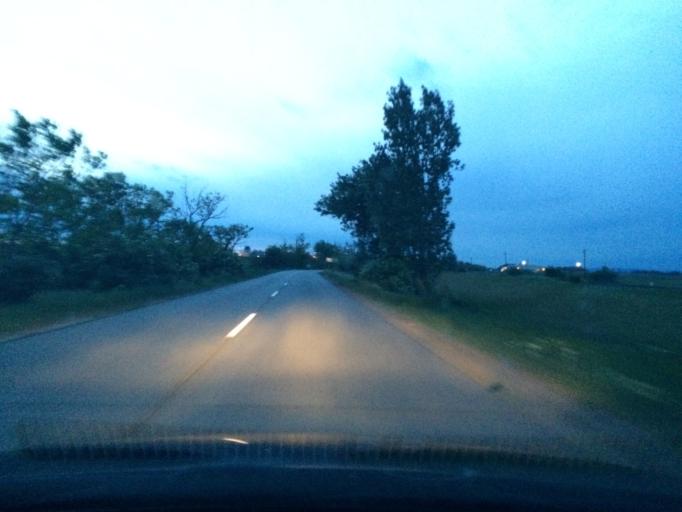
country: HU
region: Szabolcs-Szatmar-Bereg
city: Tiszavasvari
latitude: 47.9214
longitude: 21.3921
